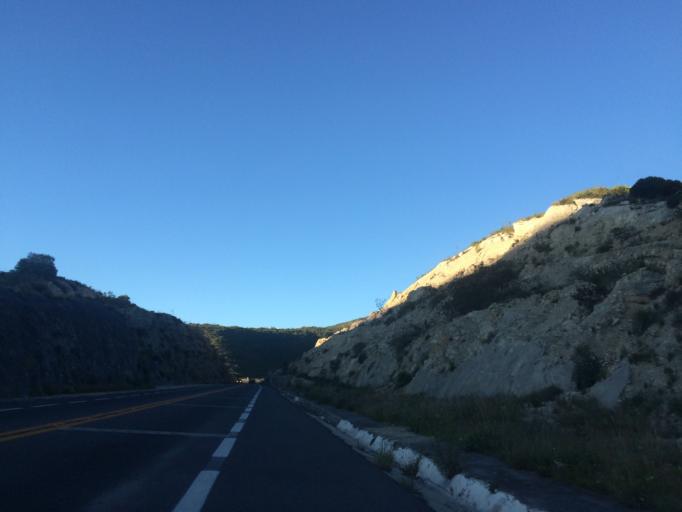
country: MX
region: Puebla
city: Chapuco
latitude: 18.6634
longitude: -97.4565
